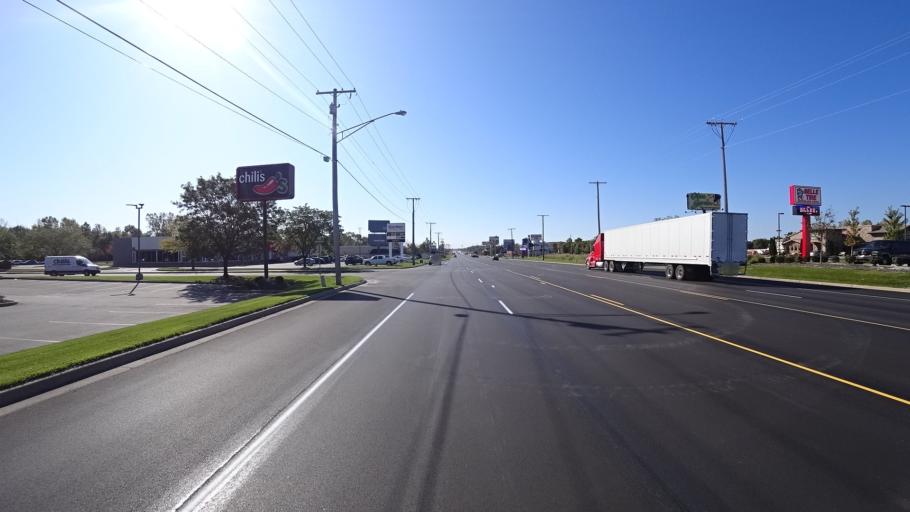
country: US
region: Indiana
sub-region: LaPorte County
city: Michigan City
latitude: 41.6707
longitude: -86.8939
